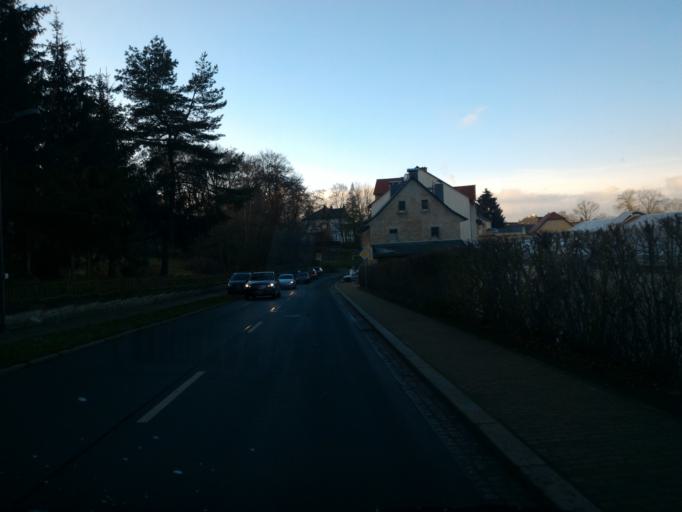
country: DE
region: Saxony
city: Grossschonau
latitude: 50.8970
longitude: 14.6585
